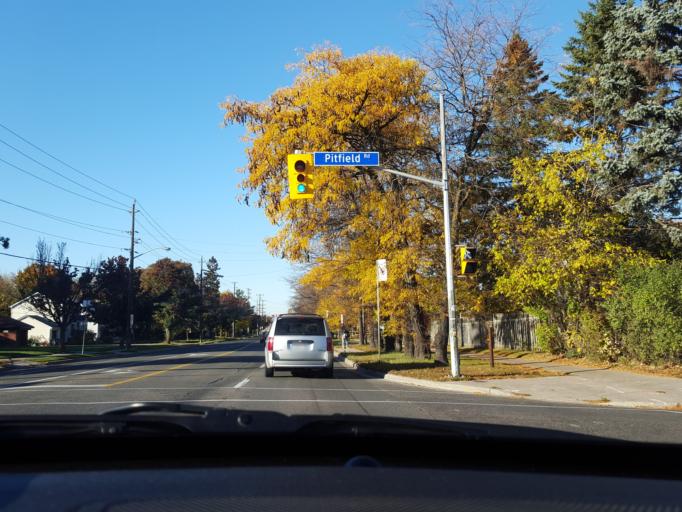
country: CA
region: Ontario
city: Scarborough
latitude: 43.7834
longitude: -79.2663
